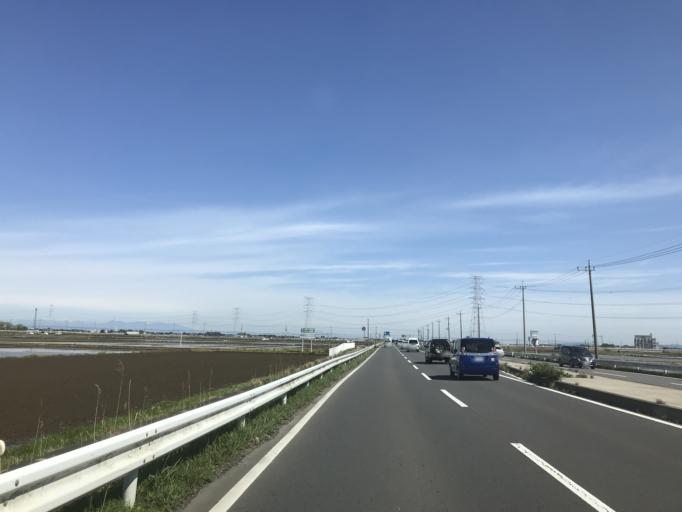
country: JP
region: Ibaraki
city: Ishige
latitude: 36.1174
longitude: 139.9830
